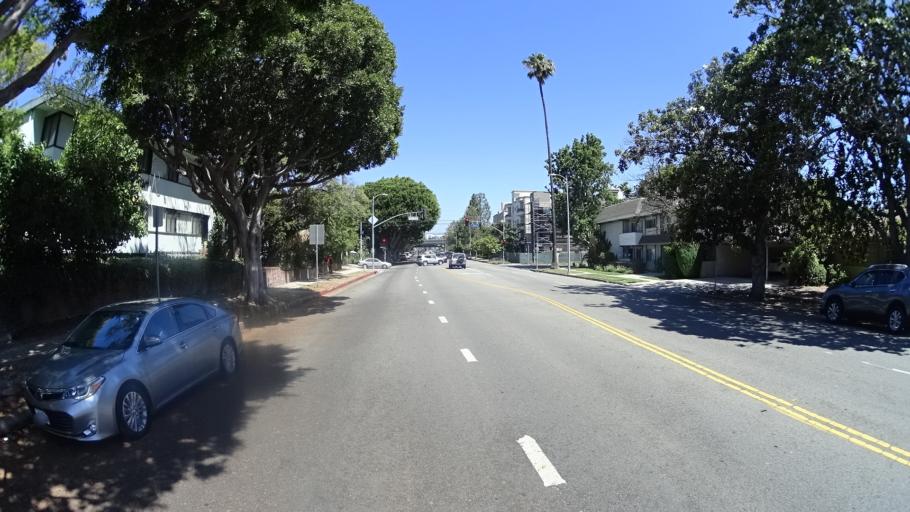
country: US
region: California
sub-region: Los Angeles County
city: Westwood, Los Angeles
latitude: 34.0252
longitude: -118.4506
